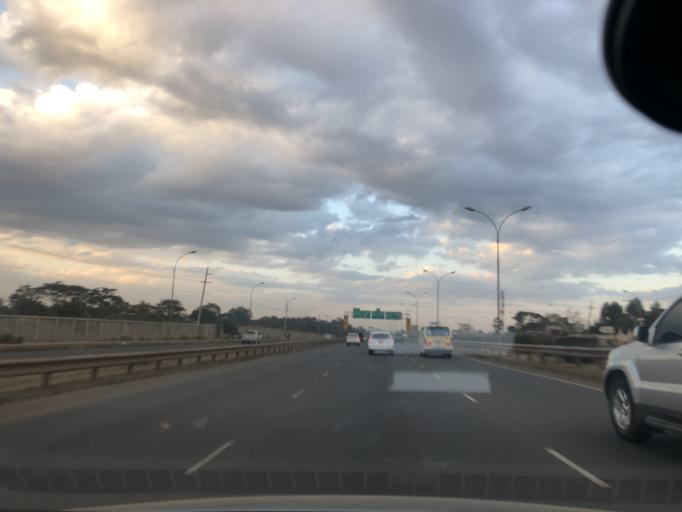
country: KE
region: Kiambu
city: Kiambu
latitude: -1.1924
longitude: 36.9275
